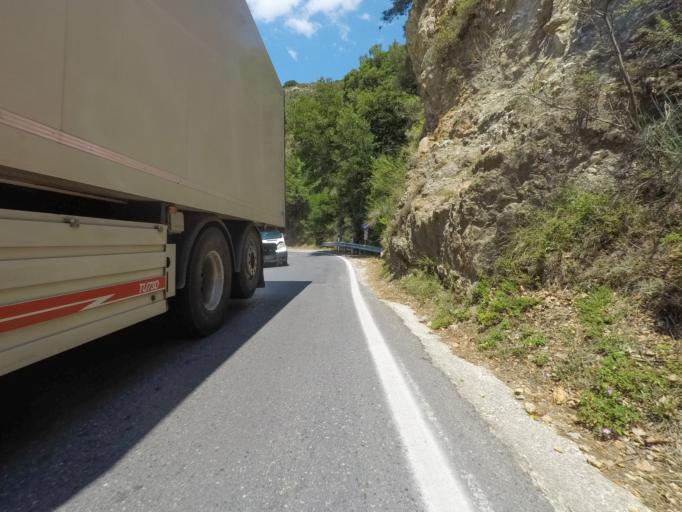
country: GR
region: Crete
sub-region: Nomos Irakleiou
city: Mokhos
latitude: 35.2214
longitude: 25.4626
